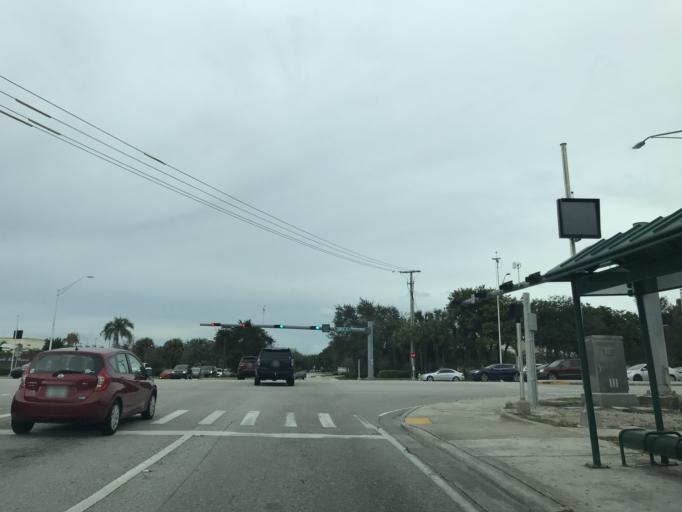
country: US
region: Florida
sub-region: Broward County
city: Margate
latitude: 26.2736
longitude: -80.2063
